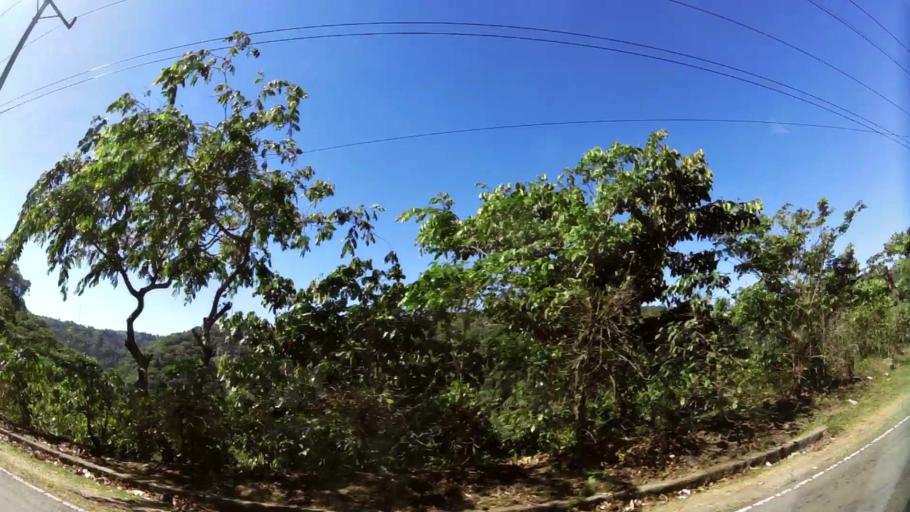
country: SV
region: Ahuachapan
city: Concepcion de Ataco
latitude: 13.8717
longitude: -89.8392
